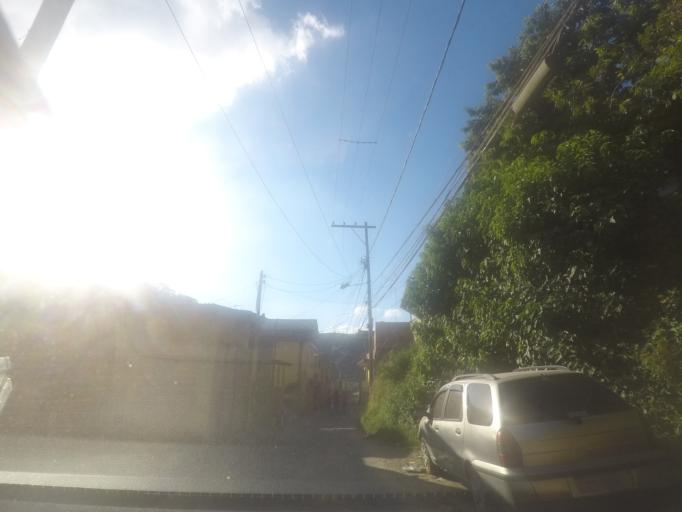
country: BR
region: Rio de Janeiro
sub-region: Petropolis
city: Petropolis
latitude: -22.5002
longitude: -43.1452
